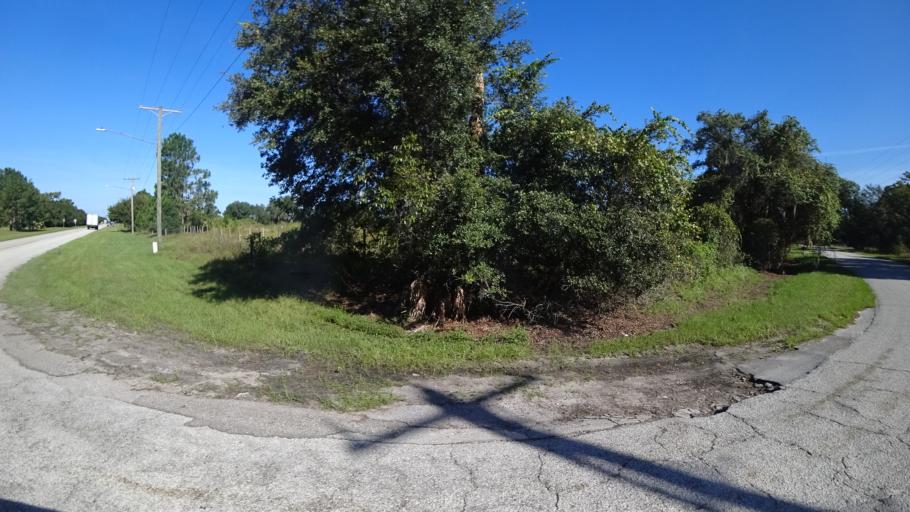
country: US
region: Florida
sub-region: Hillsborough County
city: Wimauma
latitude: 27.6540
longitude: -82.3196
